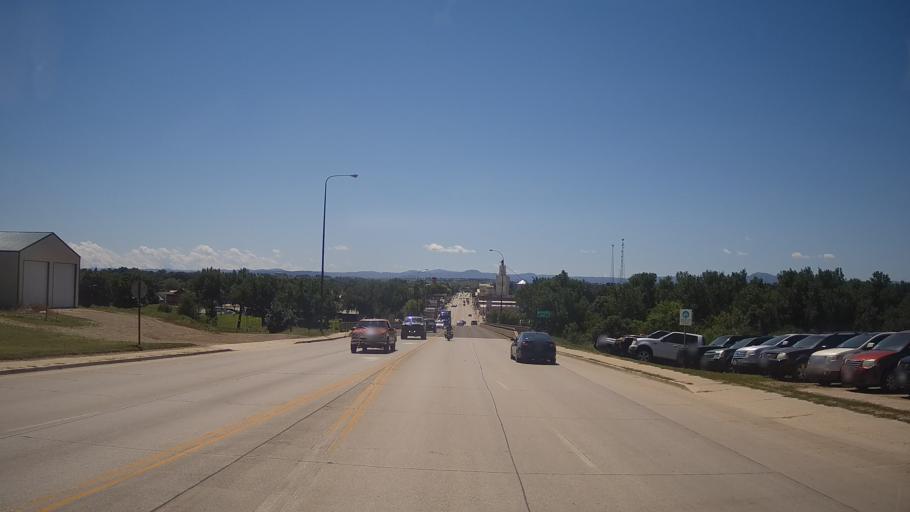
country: US
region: South Dakota
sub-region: Butte County
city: Belle Fourche
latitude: 44.6771
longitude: -103.8536
